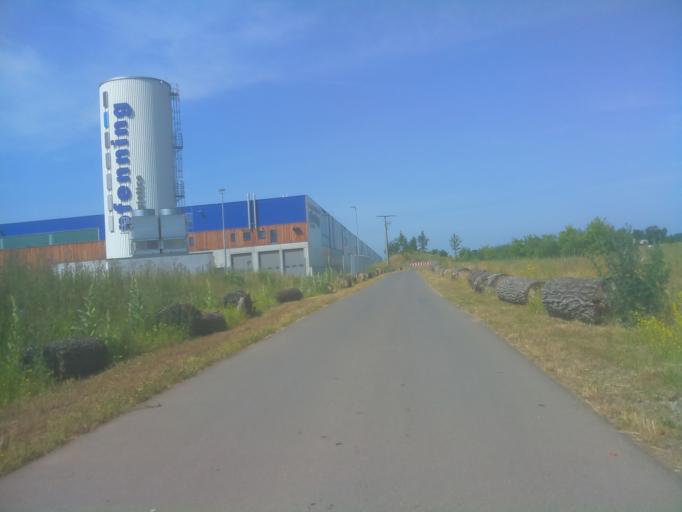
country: DE
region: Baden-Wuerttemberg
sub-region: Karlsruhe Region
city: Heddesheim
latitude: 49.5152
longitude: 8.6377
